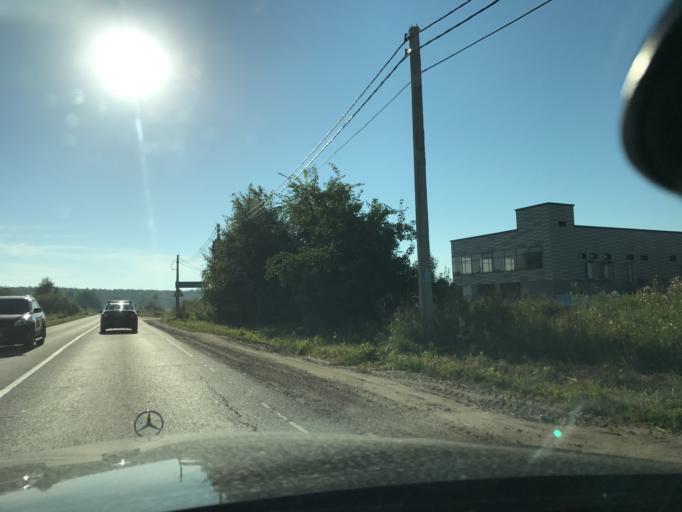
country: RU
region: Moskovskaya
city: Bakhchivandzhi
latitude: 55.8610
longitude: 38.0501
